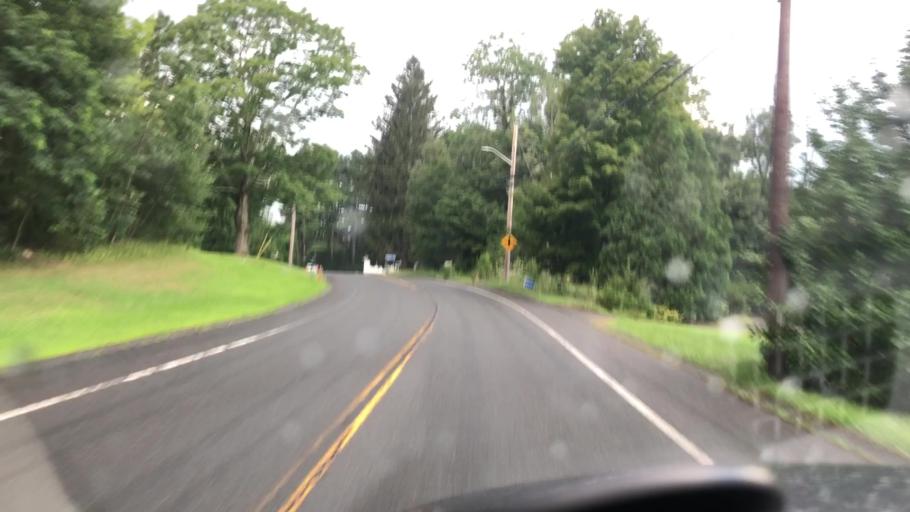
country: US
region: Massachusetts
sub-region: Hampshire County
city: Easthampton
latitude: 42.2994
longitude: -72.7150
